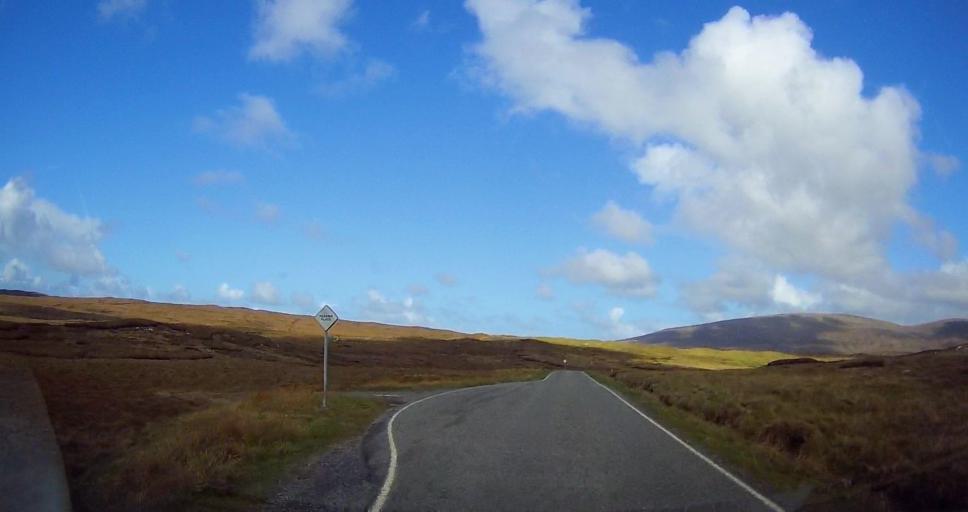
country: GB
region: Scotland
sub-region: Shetland Islands
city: Lerwick
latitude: 60.4959
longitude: -1.3932
